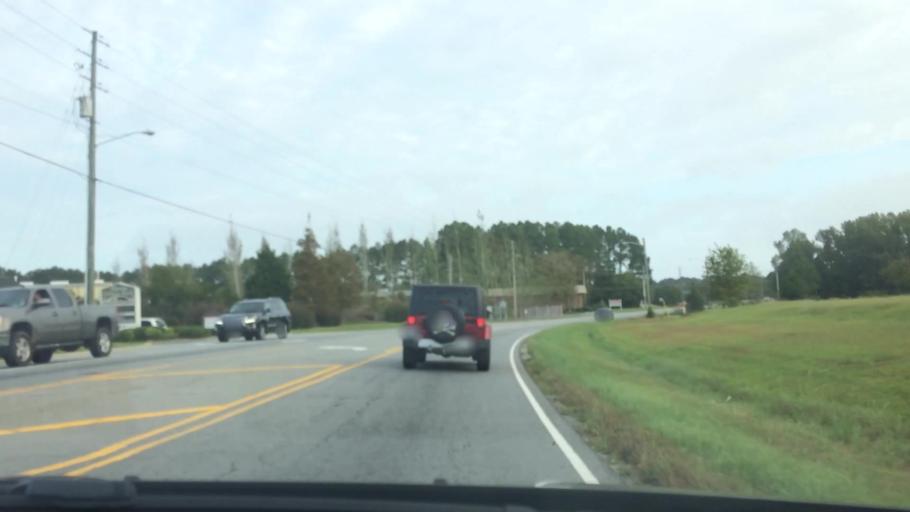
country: US
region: North Carolina
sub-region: Pitt County
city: Summerfield
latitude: 35.5599
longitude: -77.3866
